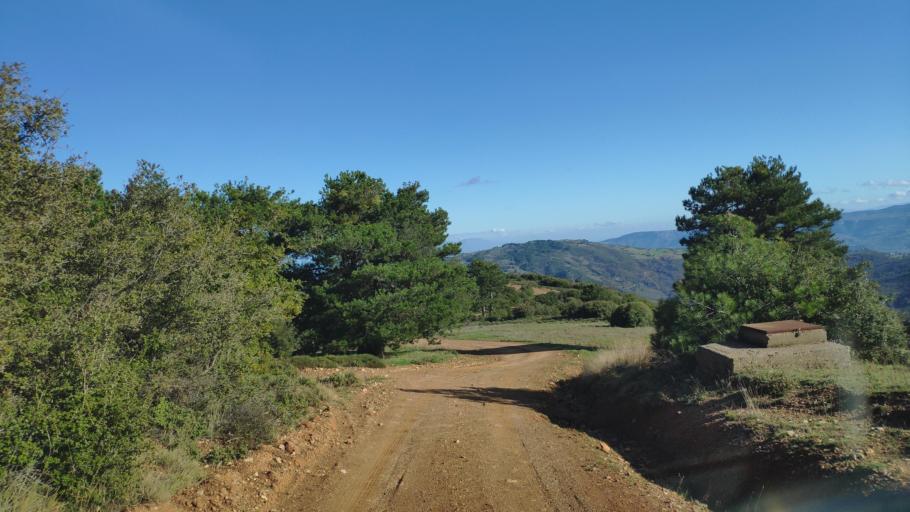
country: GR
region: West Greece
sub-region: Nomos Achaias
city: Aiyira
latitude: 38.0566
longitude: 22.4423
